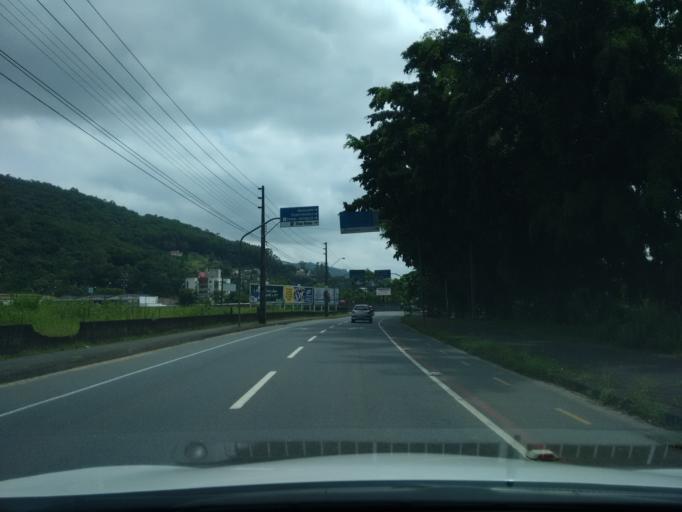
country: BR
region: Santa Catarina
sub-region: Jaragua Do Sul
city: Jaragua do Sul
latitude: -26.4926
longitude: -49.0702
